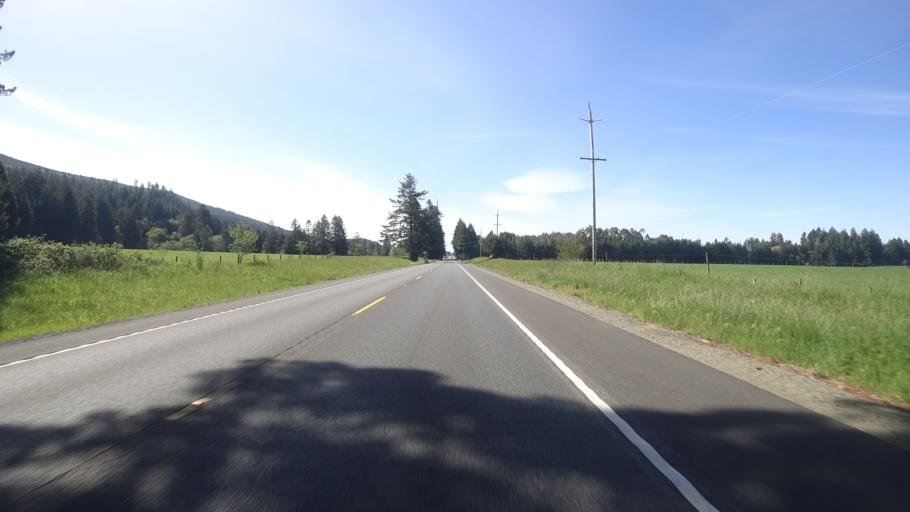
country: US
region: California
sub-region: Del Norte County
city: Bertsch-Oceanview
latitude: 41.9075
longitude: -124.1366
